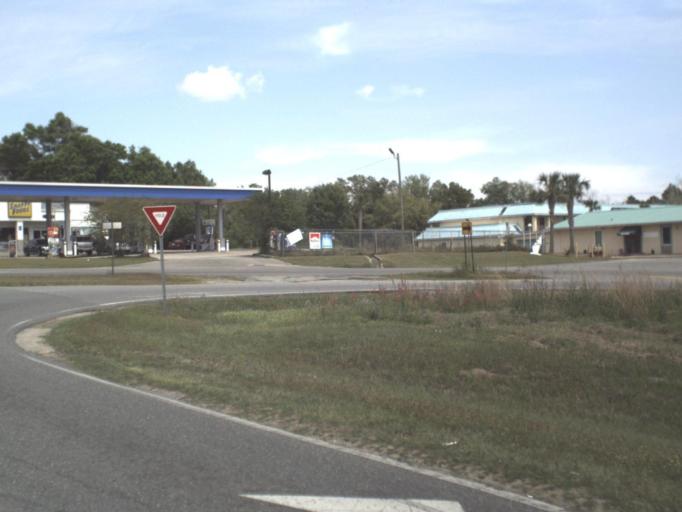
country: US
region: Florida
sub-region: Escambia County
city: Ensley
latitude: 30.5233
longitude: -87.3134
